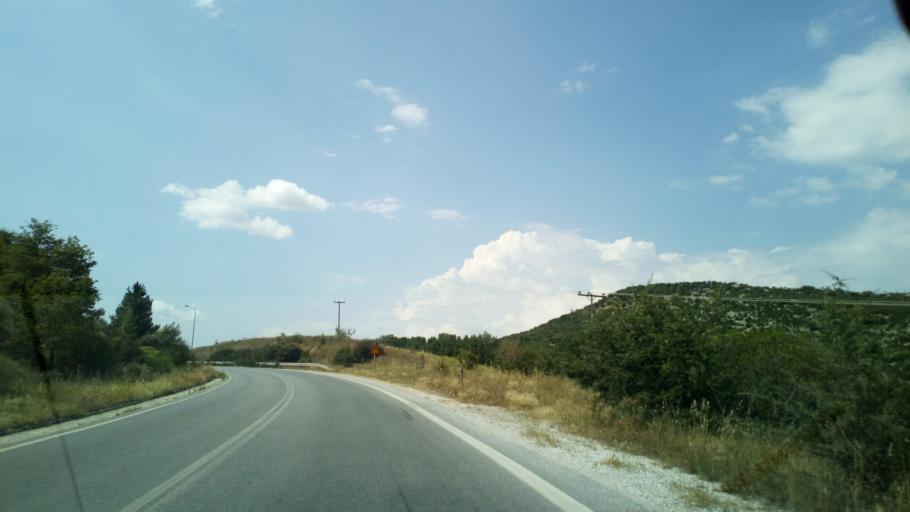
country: GR
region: Central Macedonia
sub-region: Nomos Chalkidikis
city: Polygyros
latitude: 40.4540
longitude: 23.4127
